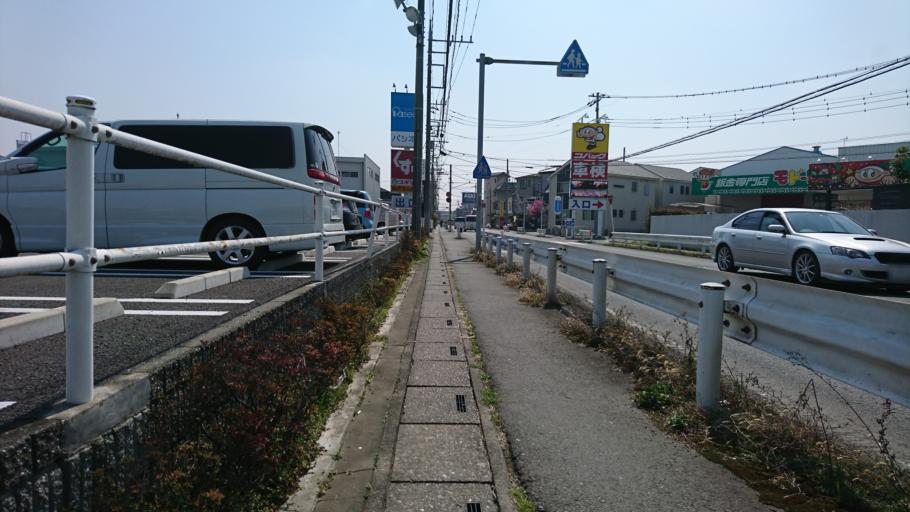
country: JP
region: Saitama
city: Kawagoe
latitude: 35.9346
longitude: 139.4789
